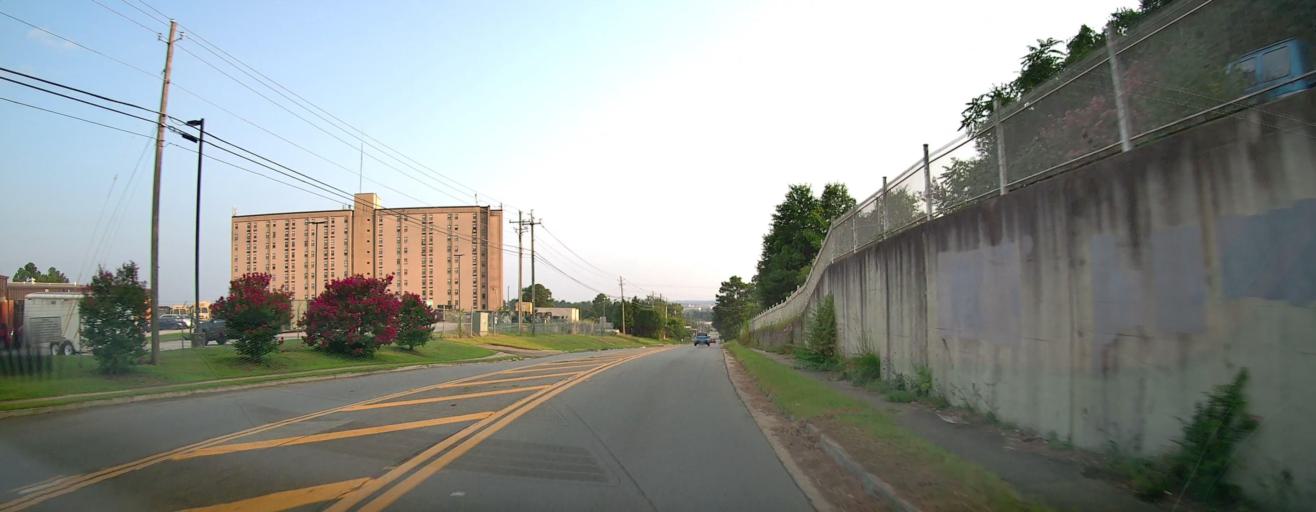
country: US
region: Georgia
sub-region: Bibb County
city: Macon
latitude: 32.8593
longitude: -83.6179
